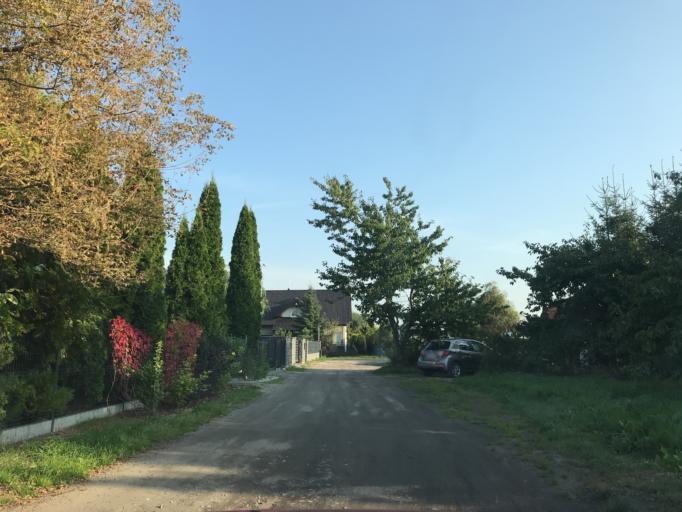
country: PL
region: Greater Poland Voivodeship
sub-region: Powiat poznanski
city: Plewiska
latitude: 52.3905
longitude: 16.8004
